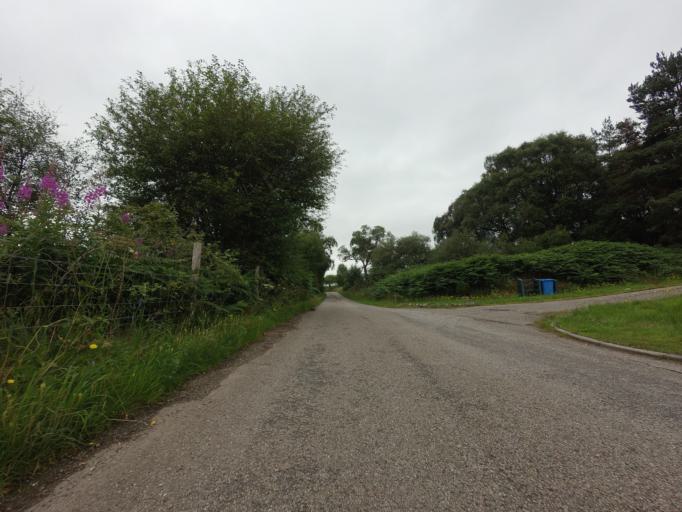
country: GB
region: Scotland
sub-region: Highland
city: Evanton
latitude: 57.9095
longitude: -4.3974
